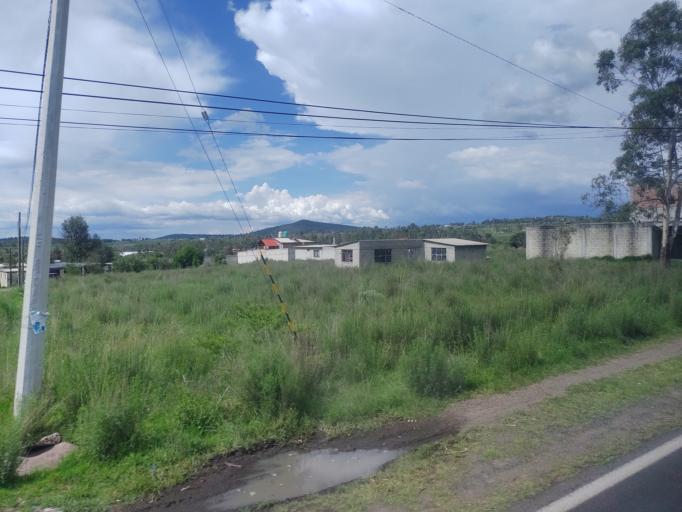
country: MX
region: Mexico
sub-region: Aculco
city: El Colorado
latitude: 20.0923
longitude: -99.7844
